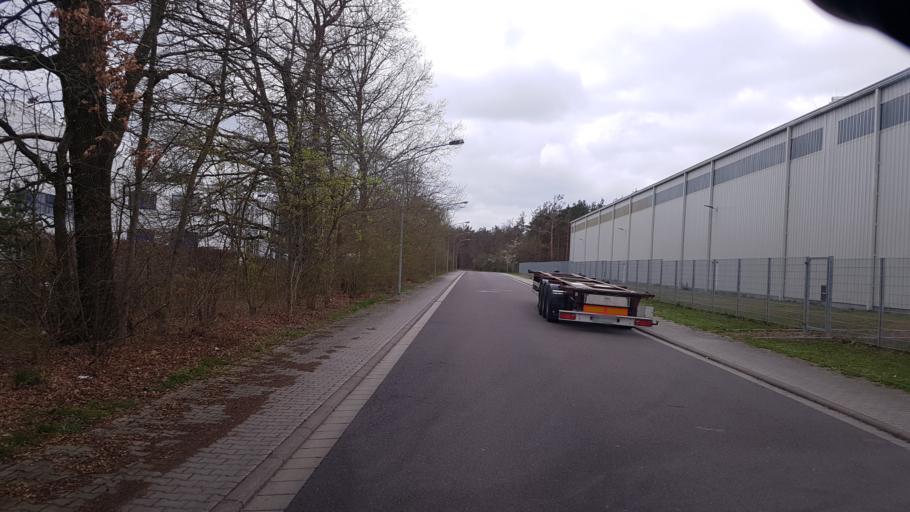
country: DE
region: Brandenburg
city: Lauchhammer
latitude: 51.4707
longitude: 13.8056
